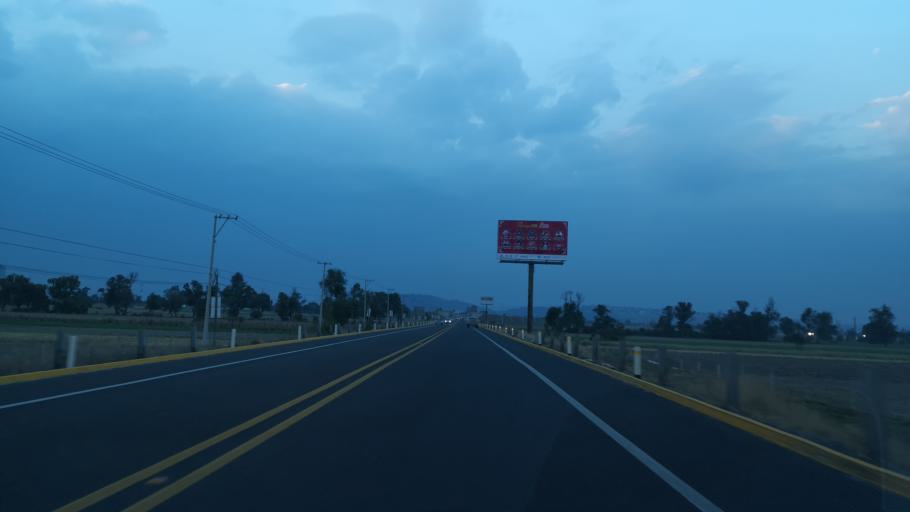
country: MX
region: Puebla
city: Santa Ana Xalmimilulco
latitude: 19.1964
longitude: -98.3652
